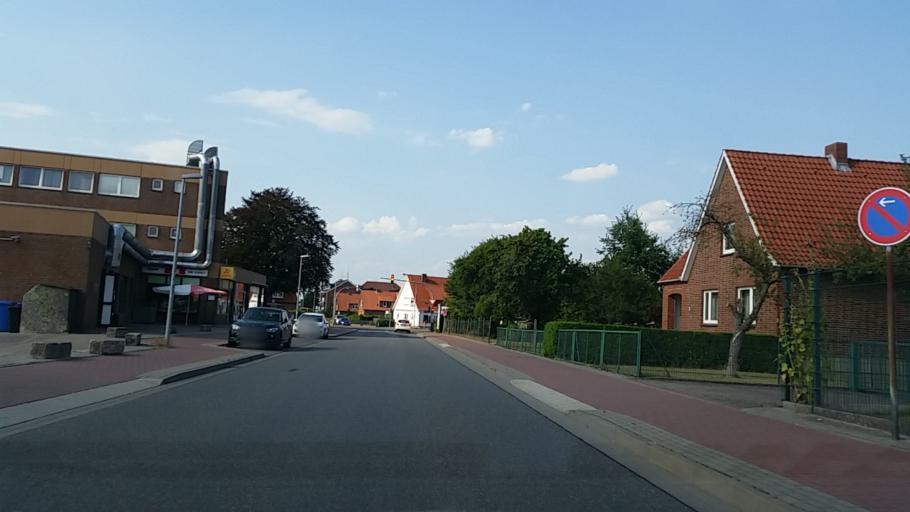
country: DE
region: Lower Saxony
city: Neu Wulmstorf
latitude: 53.4634
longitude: 9.8005
